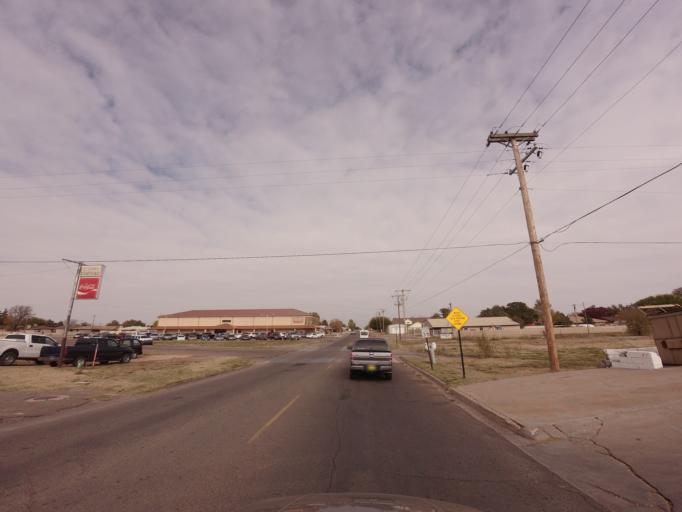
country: US
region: New Mexico
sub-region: Curry County
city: Clovis
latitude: 34.4198
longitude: -103.2141
